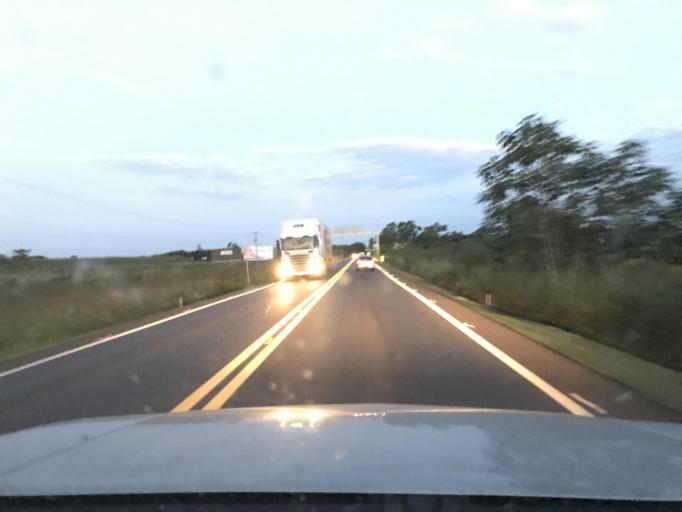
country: PY
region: Canindeyu
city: Salto del Guaira
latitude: -24.0394
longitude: -54.2794
